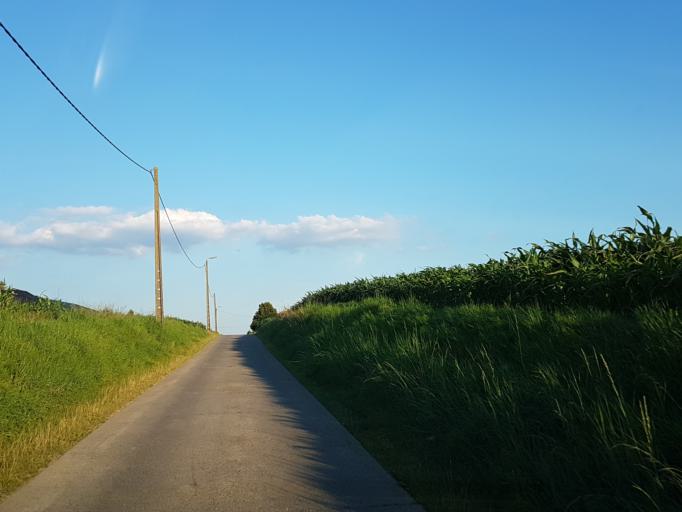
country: BE
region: Flanders
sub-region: Provincie Vlaams-Brabant
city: Merchtem
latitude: 50.9089
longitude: 4.2552
